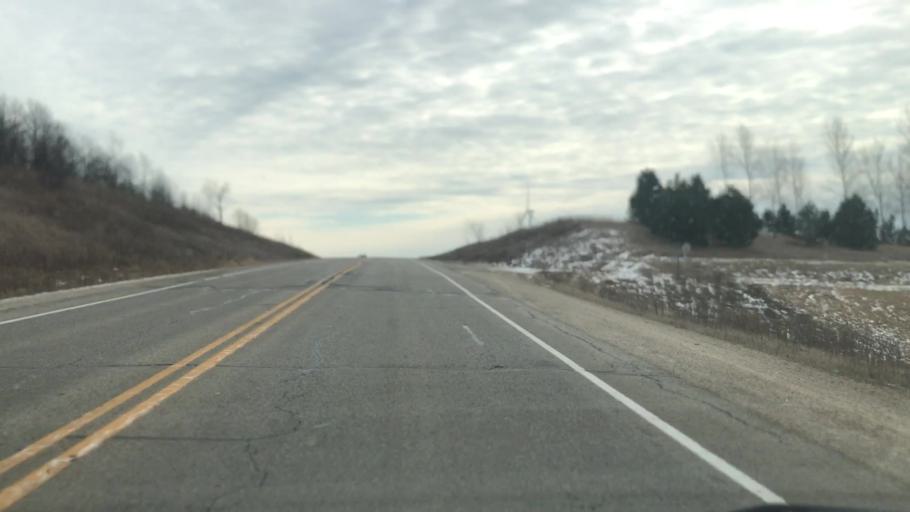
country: US
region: Wisconsin
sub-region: Dodge County
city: Theresa
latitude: 43.4381
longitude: -88.4775
